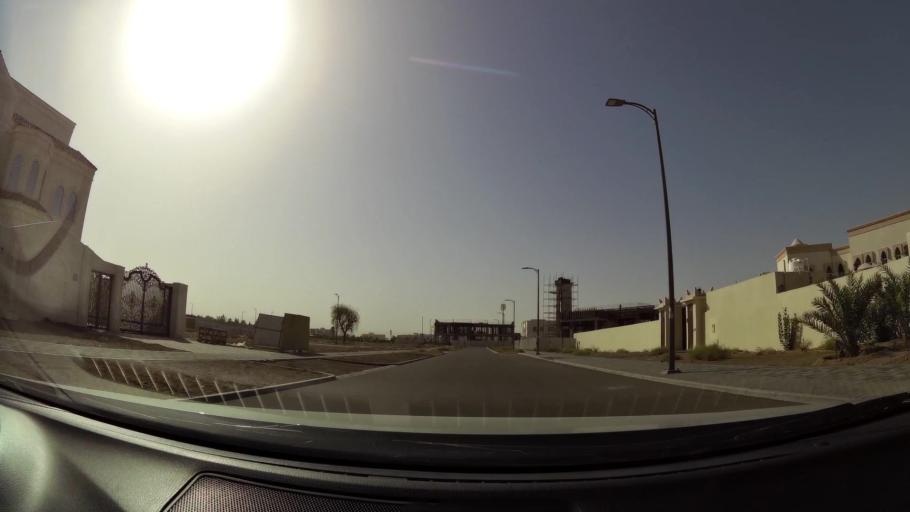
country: OM
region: Al Buraimi
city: Al Buraymi
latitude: 24.3591
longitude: 55.7903
